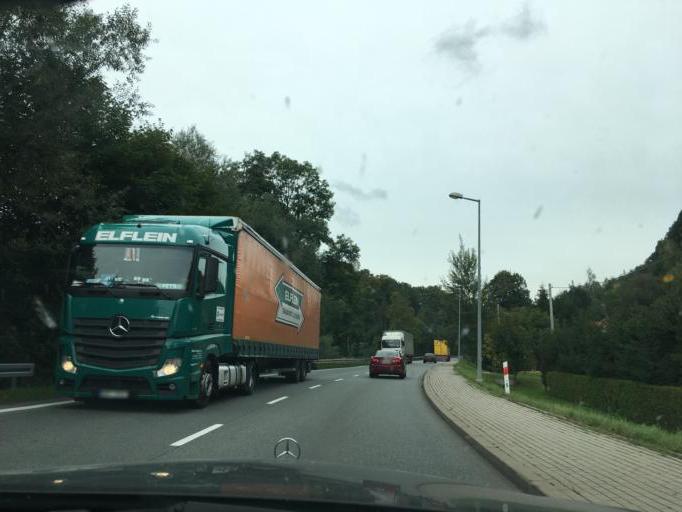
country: PL
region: Lower Silesian Voivodeship
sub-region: Powiat klodzki
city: Lewin Klodzki
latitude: 50.4127
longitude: 16.2676
